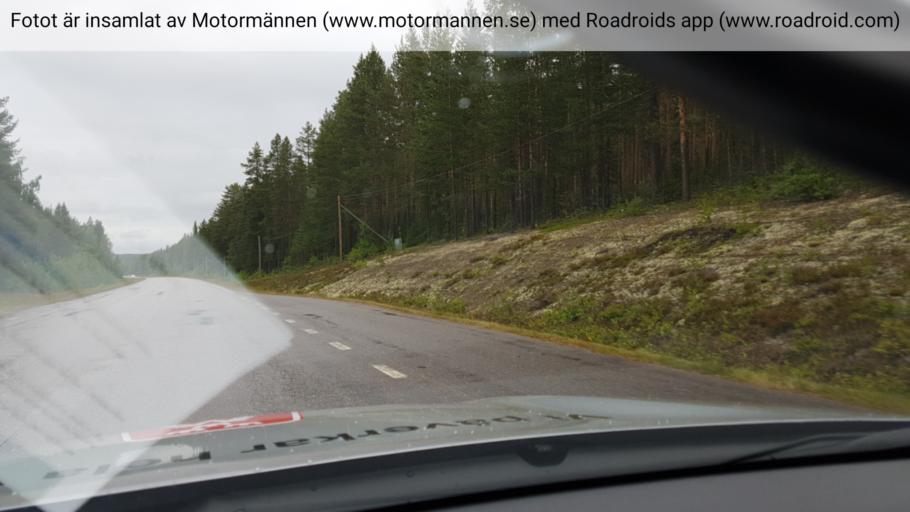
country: SE
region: Norrbotten
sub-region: Alvsbyns Kommun
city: AElvsbyn
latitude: 66.1223
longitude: 20.9199
